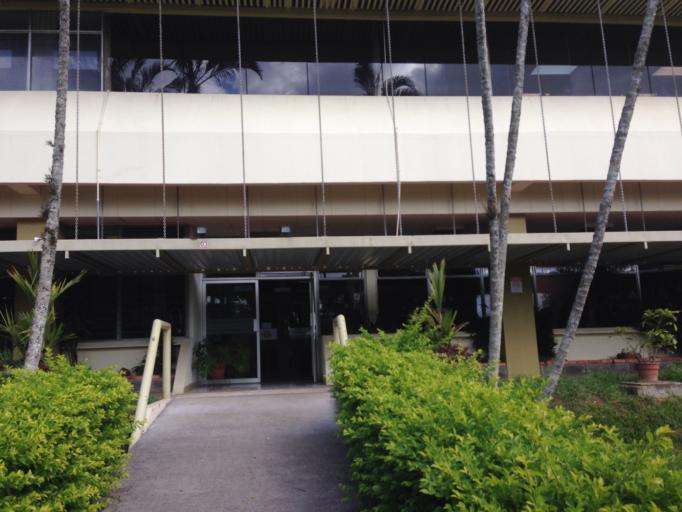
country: CR
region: San Jose
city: Sabanilla
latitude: 9.9398
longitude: -84.0457
